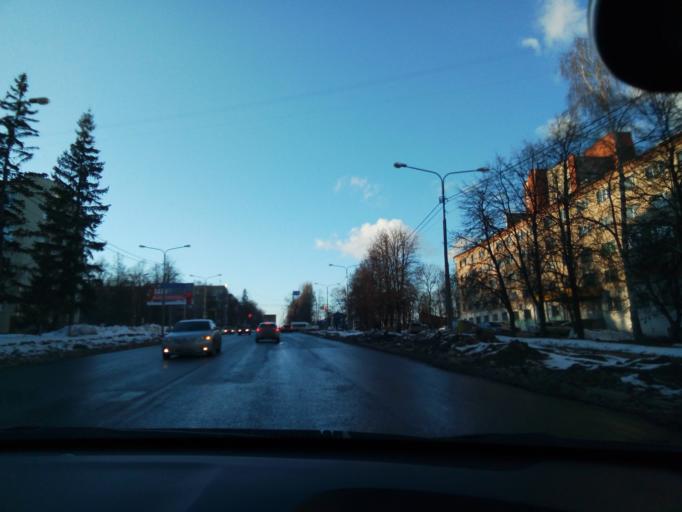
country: RU
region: Chuvashia
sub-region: Cheboksarskiy Rayon
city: Cheboksary
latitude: 56.1399
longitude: 47.1994
